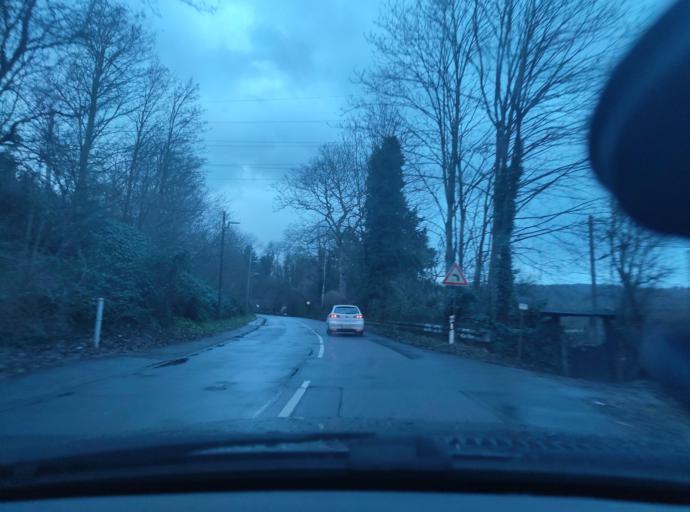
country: DE
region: North Rhine-Westphalia
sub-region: Regierungsbezirk Dusseldorf
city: Essen
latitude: 51.4271
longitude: 7.0686
